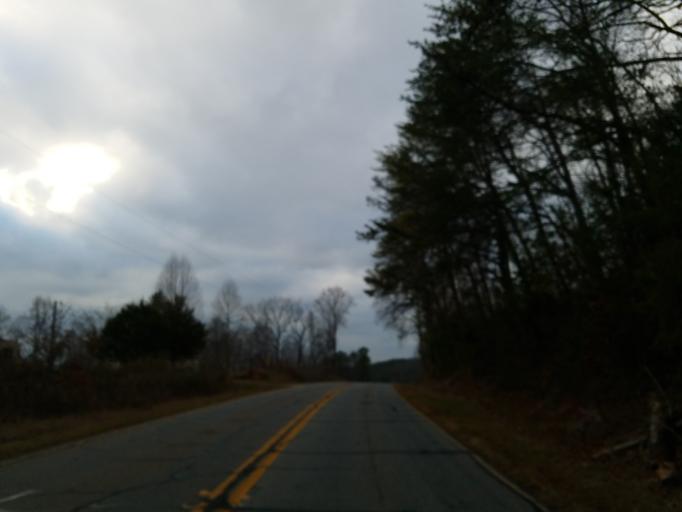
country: US
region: Georgia
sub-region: Bartow County
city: Rydal
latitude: 34.3454
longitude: -84.7054
